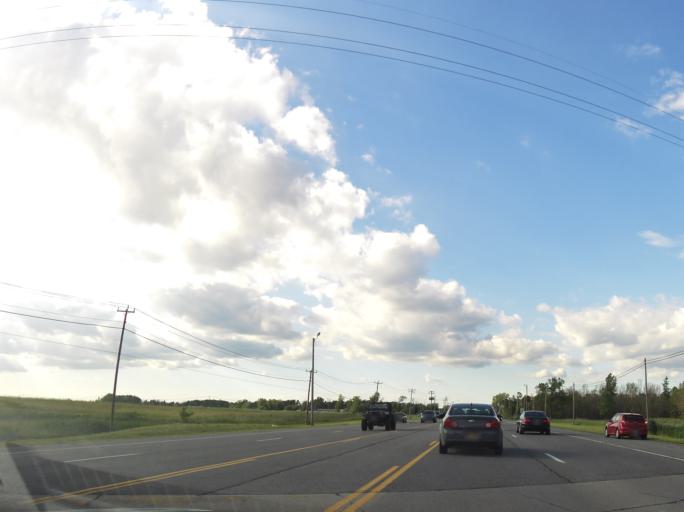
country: US
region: New York
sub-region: Erie County
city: Harris Hill
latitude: 42.9416
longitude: -78.6969
